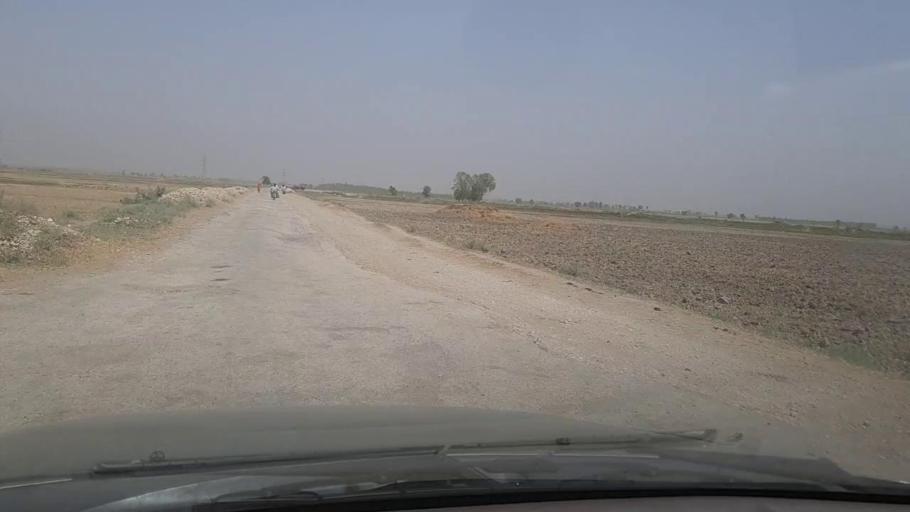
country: PK
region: Sindh
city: Madeji
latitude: 27.8072
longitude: 68.3992
